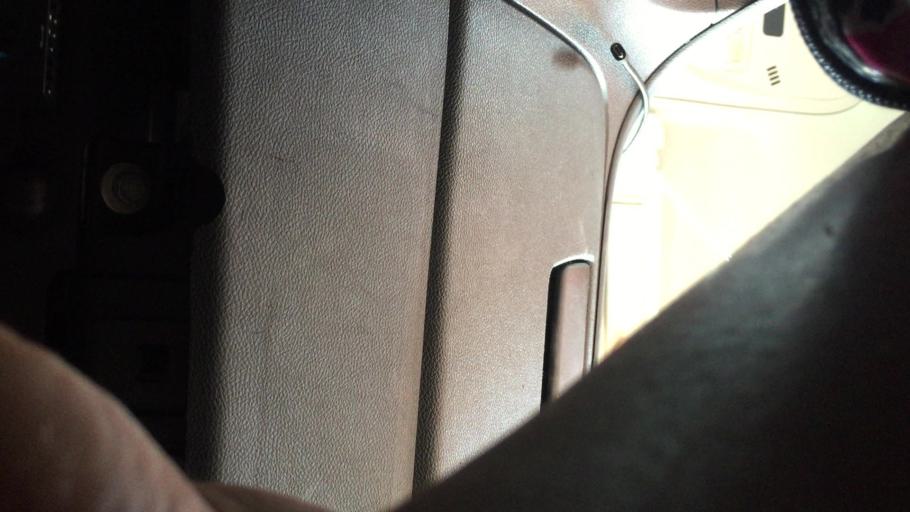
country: US
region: Georgia
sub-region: Carroll County
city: Carrollton
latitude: 33.6036
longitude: -85.0257
